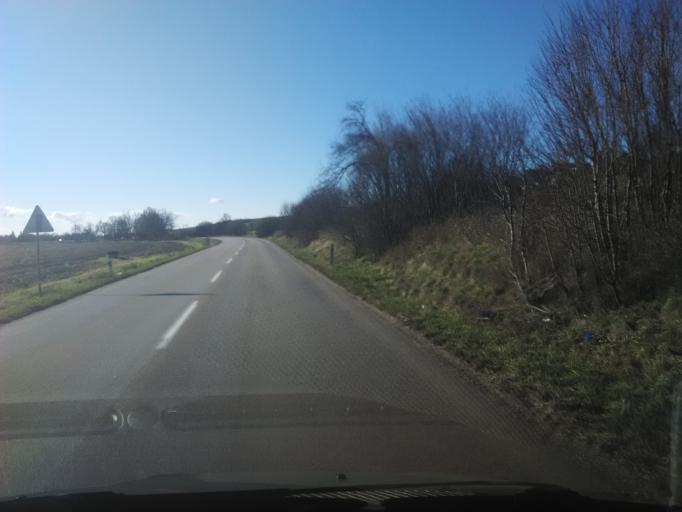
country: SK
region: Nitriansky
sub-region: Okres Nitra
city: Vrable
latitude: 48.2449
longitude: 18.2892
